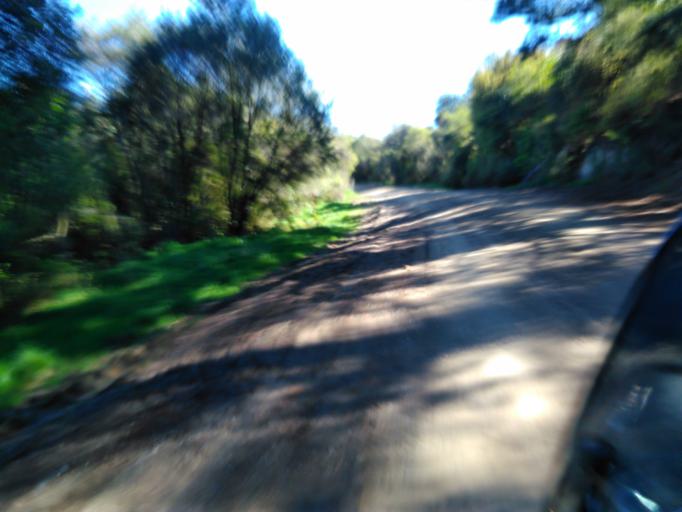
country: NZ
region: Gisborne
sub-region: Gisborne District
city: Gisborne
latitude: -38.3884
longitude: 177.6255
